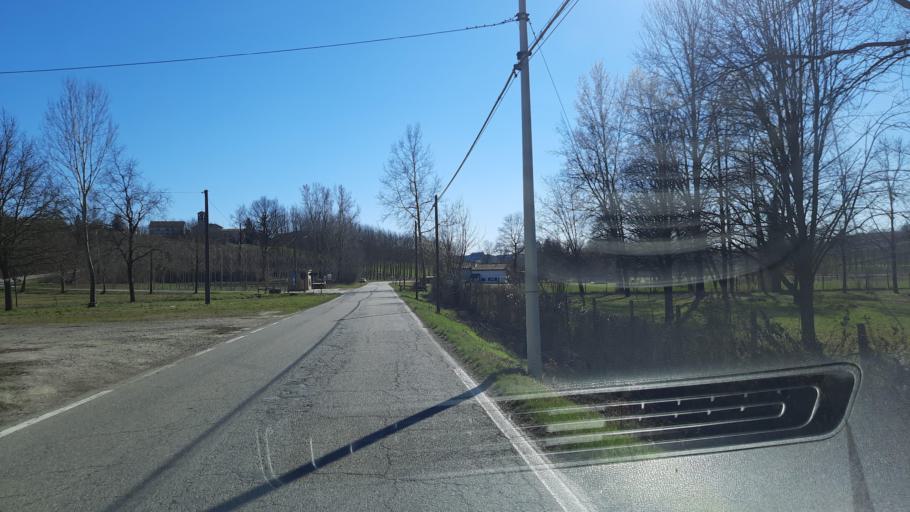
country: IT
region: Piedmont
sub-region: Provincia di Alessandria
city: Cella Monte
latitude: 45.0658
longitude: 8.4020
